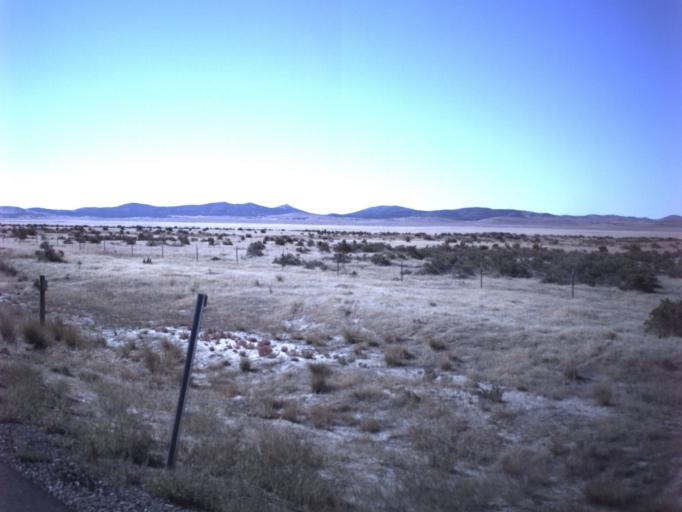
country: US
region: Utah
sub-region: Tooele County
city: Grantsville
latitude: 40.3253
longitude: -112.7441
